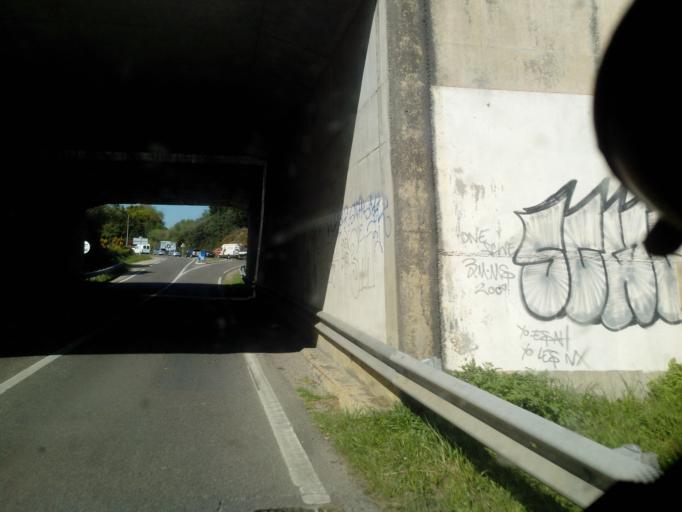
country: FR
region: Pays de la Loire
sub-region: Departement de la Loire-Atlantique
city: Pornic
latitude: 47.1106
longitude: -2.0743
